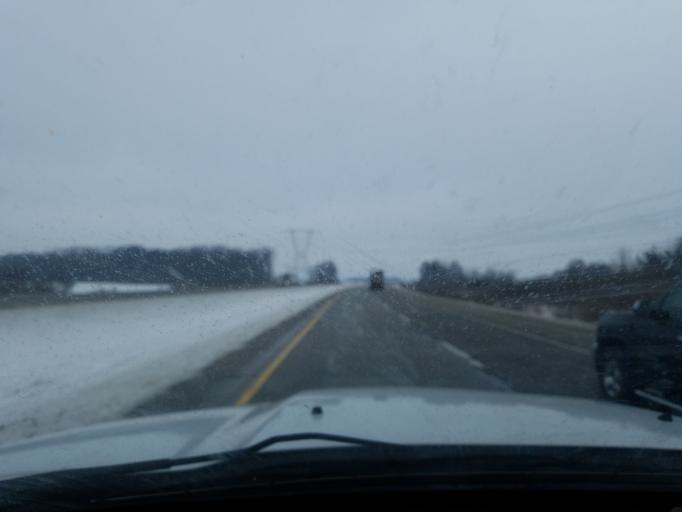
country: US
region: Indiana
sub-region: Marshall County
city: Argos
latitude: 41.2041
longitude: -86.2582
